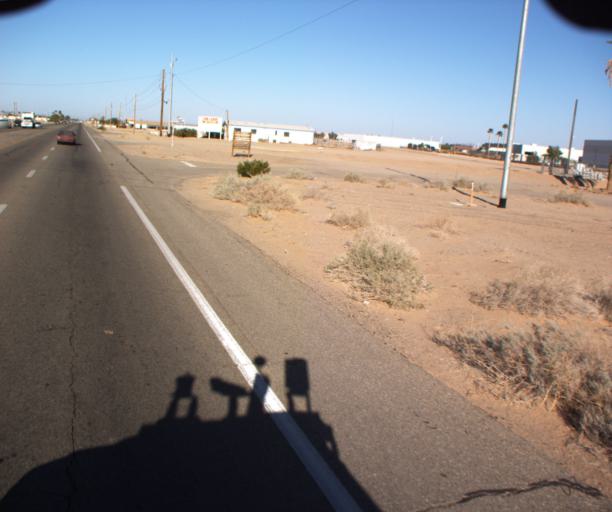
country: US
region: Arizona
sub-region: Yuma County
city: Fortuna Foothills
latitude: 32.6704
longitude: -114.4998
